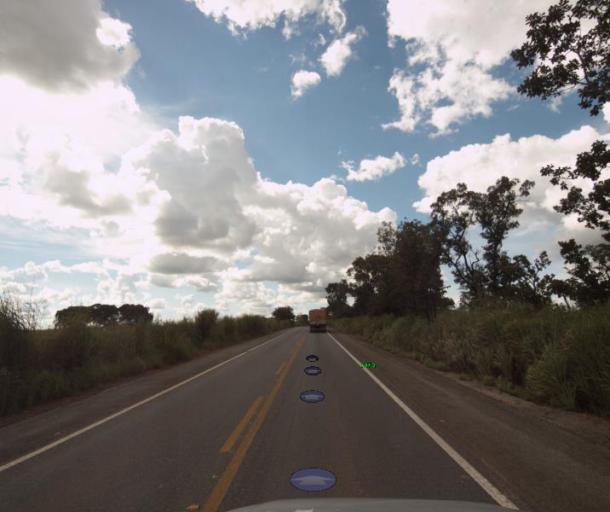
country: BR
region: Goias
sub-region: Porangatu
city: Porangatu
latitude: -13.2303
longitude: -49.1455
